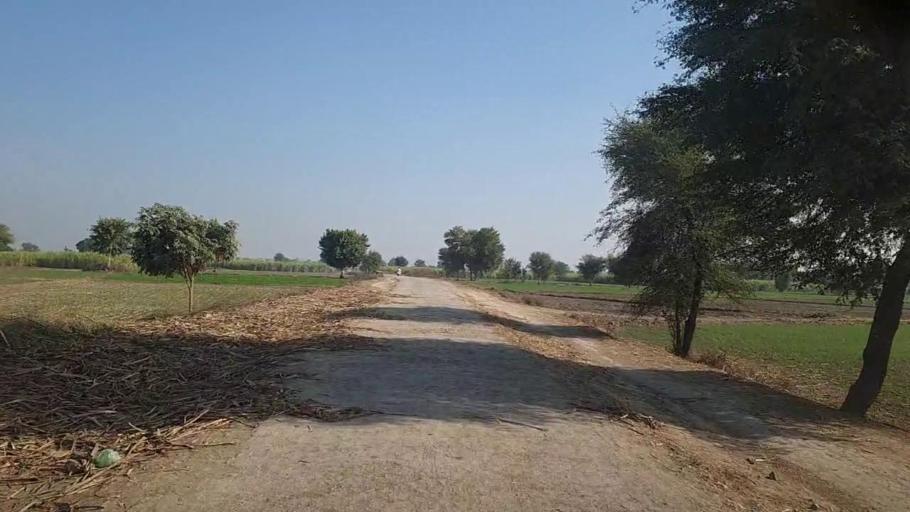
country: PK
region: Sindh
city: Darya Khan Marri
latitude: 26.6707
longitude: 68.3279
